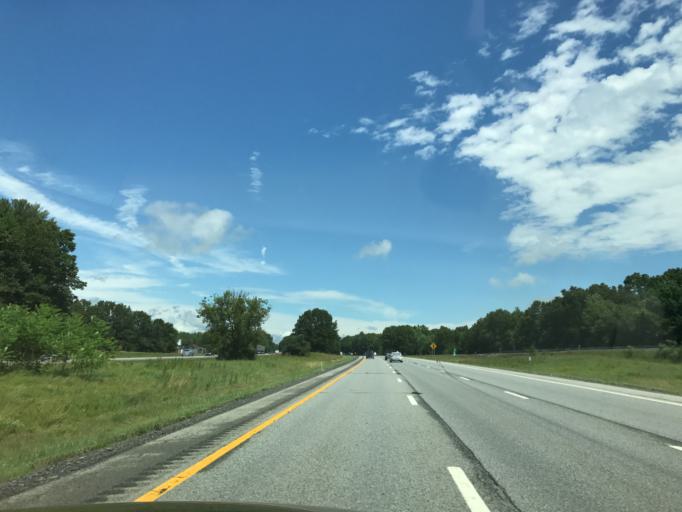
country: US
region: New York
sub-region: Saratoga County
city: Saratoga Springs
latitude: 43.1691
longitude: -73.7124
